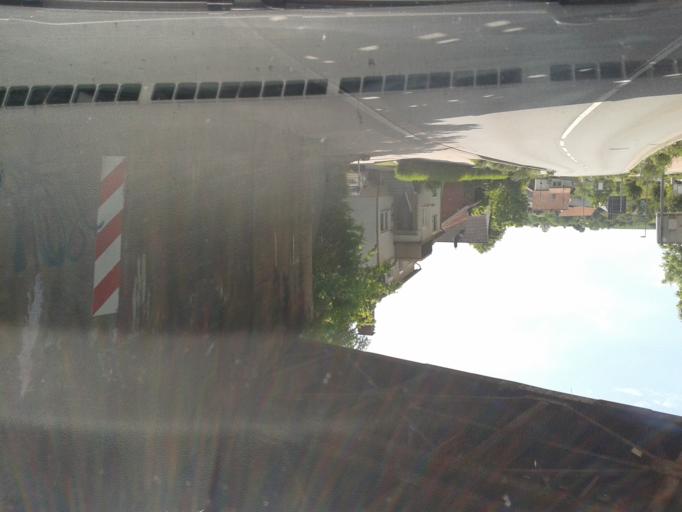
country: DE
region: North Rhine-Westphalia
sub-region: Regierungsbezirk Detmold
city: Lugde
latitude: 51.9526
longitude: 9.2431
